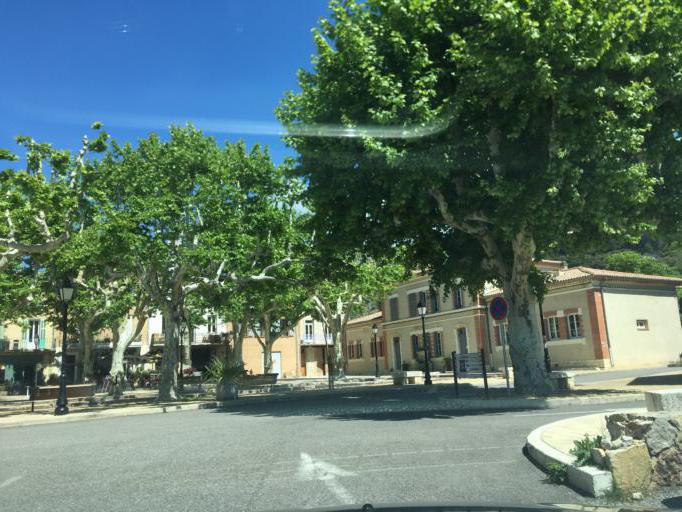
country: FR
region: Provence-Alpes-Cote d'Azur
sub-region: Departement du Var
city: Villecroze
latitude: 43.5825
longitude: 6.2764
